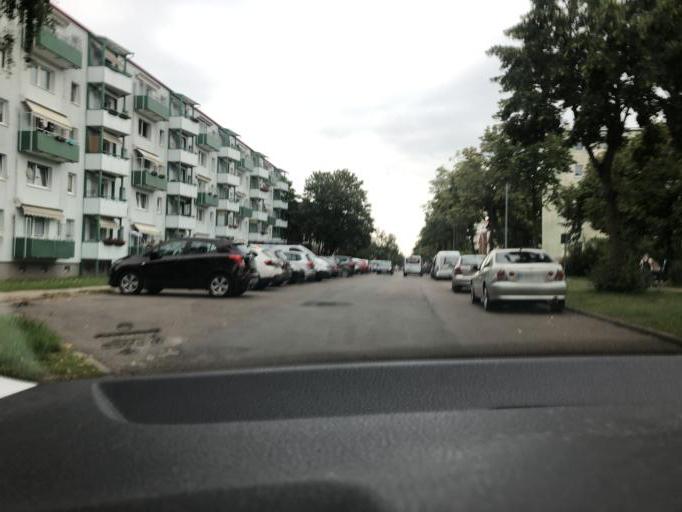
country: DE
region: Mecklenburg-Vorpommern
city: Lankow
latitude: 53.6481
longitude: 11.3682
